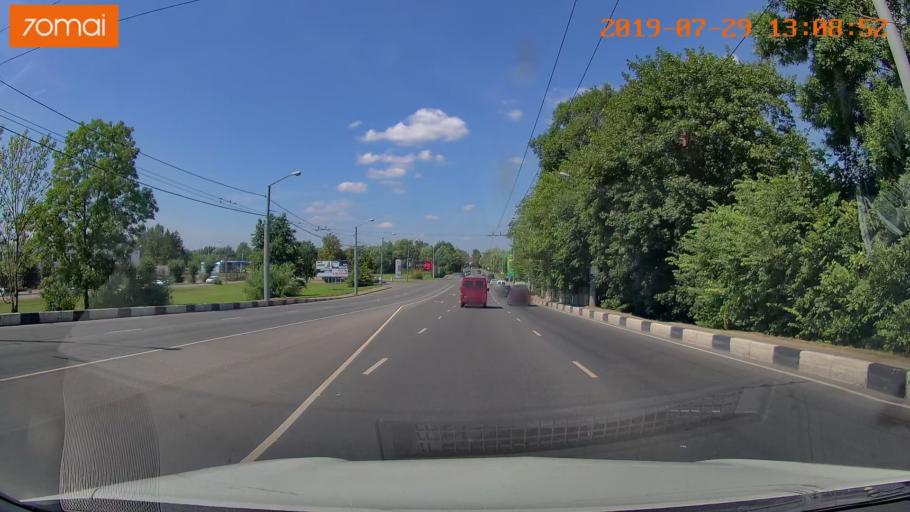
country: RU
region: Kaliningrad
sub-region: Gorod Kaliningrad
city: Kaliningrad
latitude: 54.7125
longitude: 20.4248
